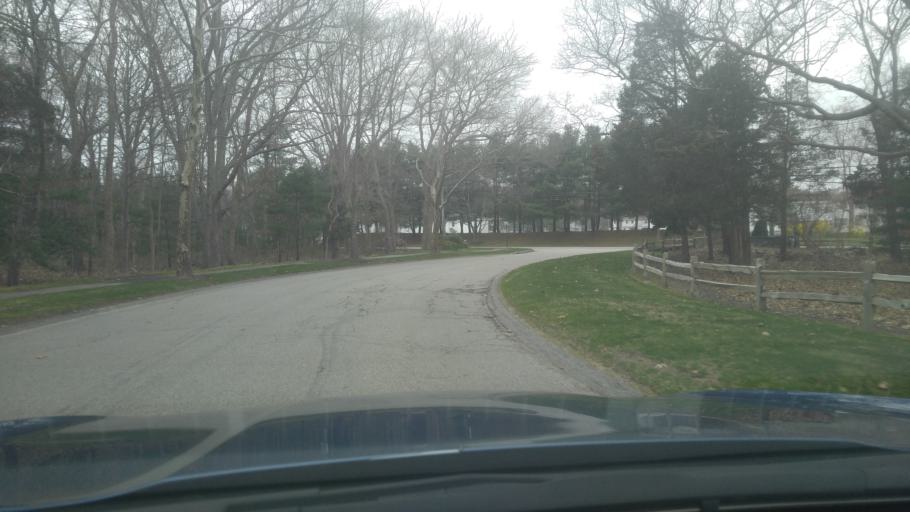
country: US
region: Rhode Island
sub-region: Washington County
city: North Kingstown
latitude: 41.5925
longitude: -71.4455
